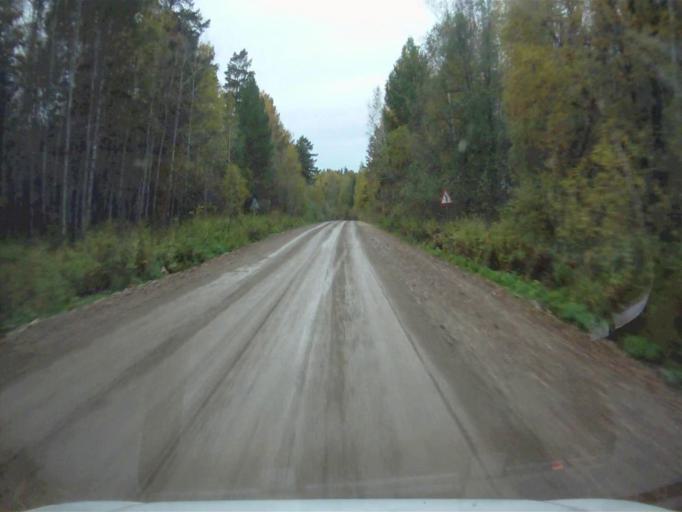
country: RU
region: Chelyabinsk
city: Nyazepetrovsk
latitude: 56.1025
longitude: 59.3872
